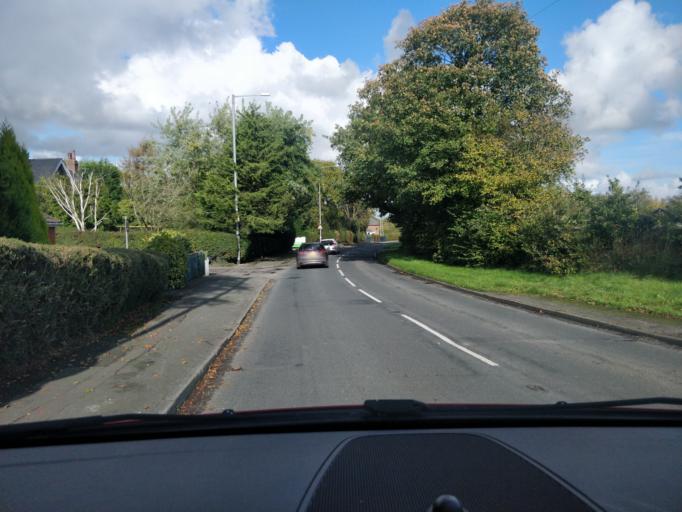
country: GB
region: England
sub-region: Lancashire
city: Parbold
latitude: 53.5911
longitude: -2.8211
